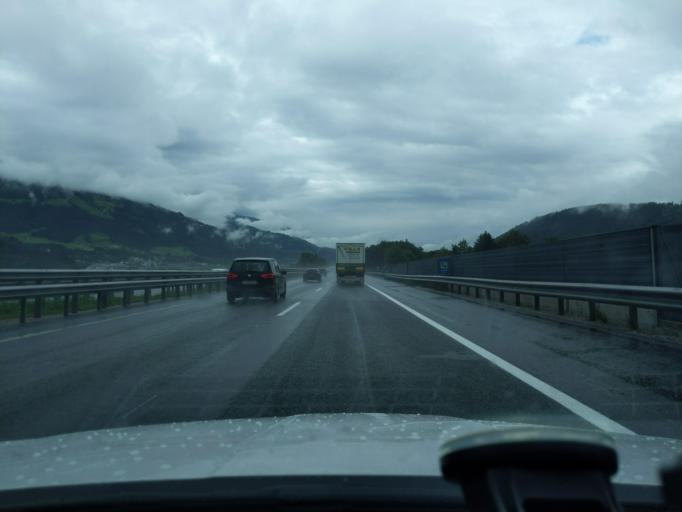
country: AT
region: Tyrol
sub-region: Politischer Bezirk Schwaz
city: Terfens
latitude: 47.3219
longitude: 11.6639
